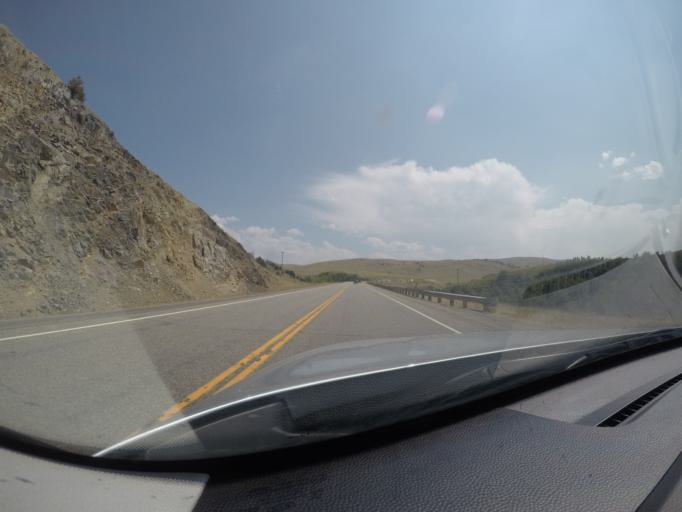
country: US
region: Montana
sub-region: Madison County
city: Virginia City
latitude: 45.5211
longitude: -111.6924
